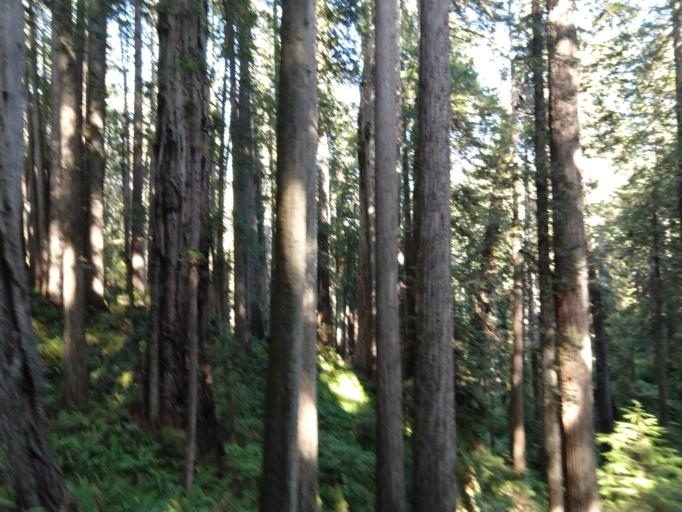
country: US
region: California
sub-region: Humboldt County
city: Westhaven-Moonstone
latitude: 41.3892
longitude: -124.0525
